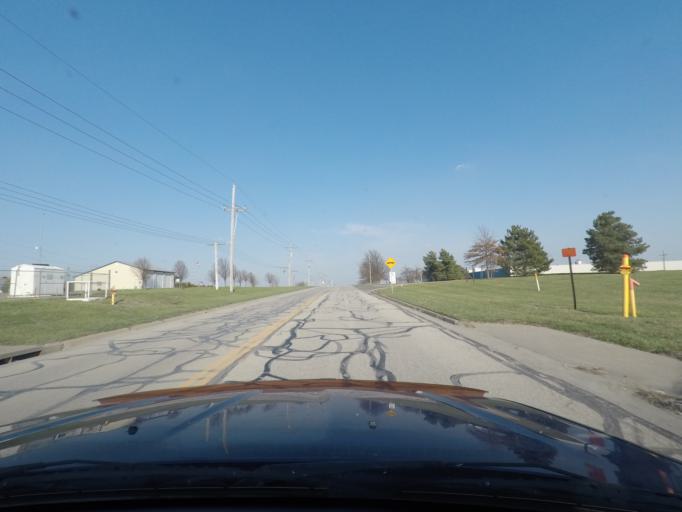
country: US
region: Kansas
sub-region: Douglas County
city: Lawrence
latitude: 39.0006
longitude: -95.2736
